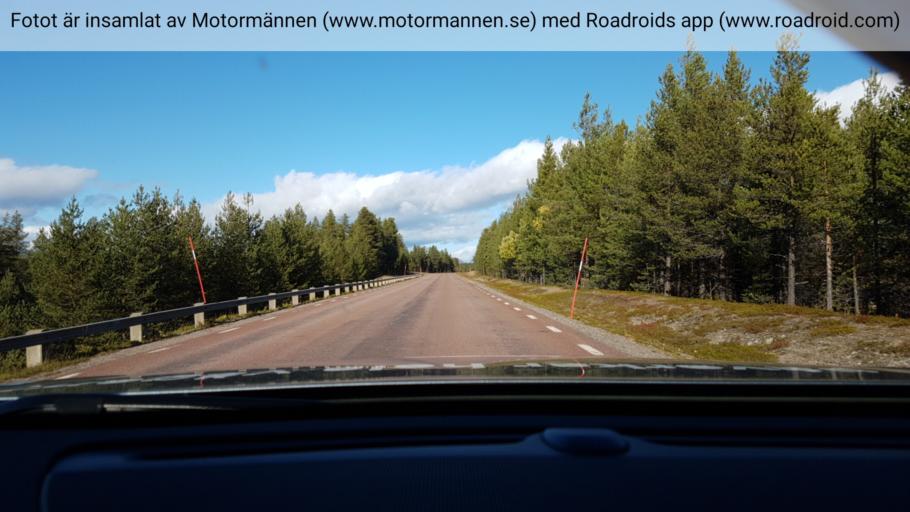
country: SE
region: Norrbotten
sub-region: Arjeplogs Kommun
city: Arjeplog
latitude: 66.0253
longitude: 18.0663
